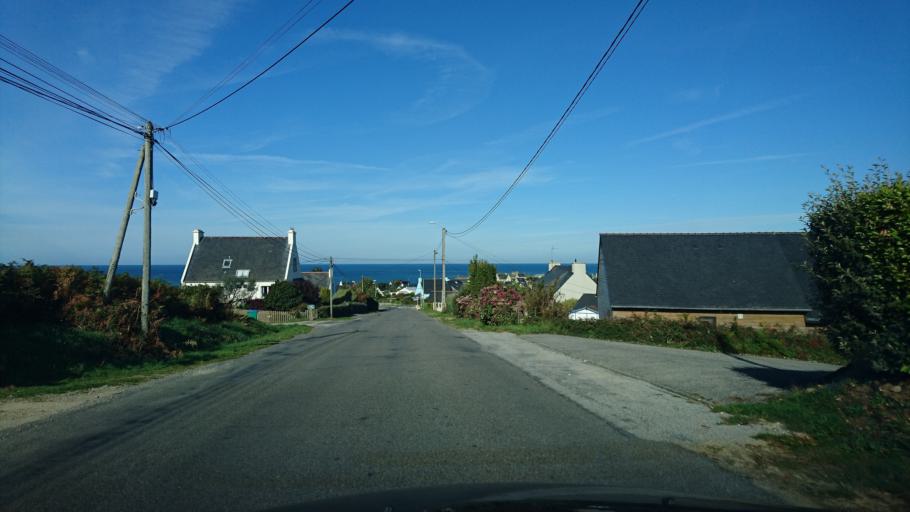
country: FR
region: Brittany
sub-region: Departement du Finistere
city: Lampaul-Plouarzel
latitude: 48.4350
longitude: -4.7732
